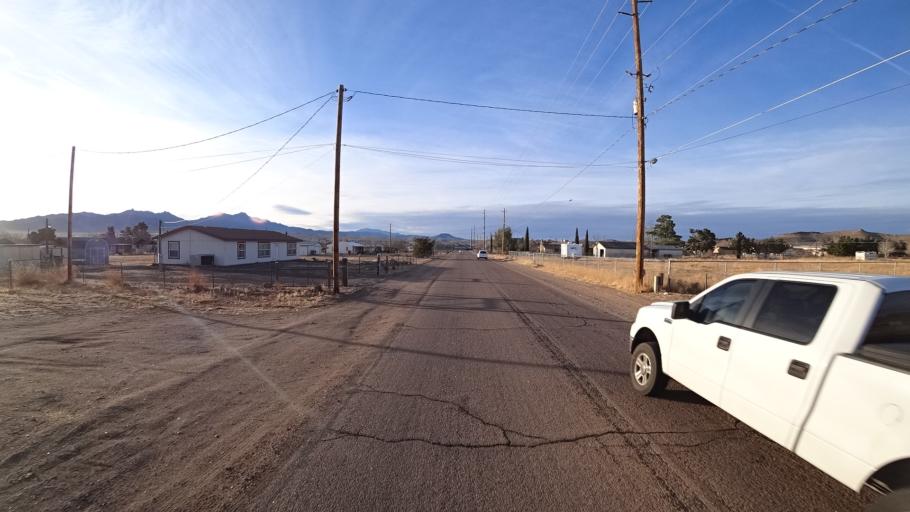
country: US
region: Arizona
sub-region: Mohave County
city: New Kingman-Butler
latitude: 35.2423
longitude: -114.0333
